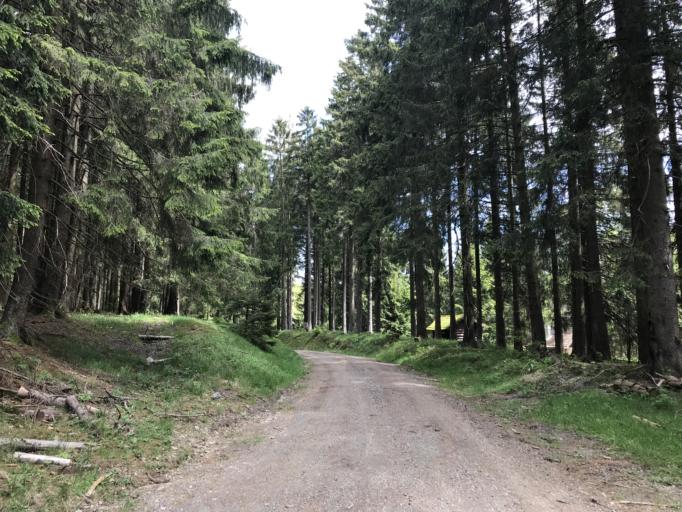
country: DE
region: Lower Saxony
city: Sankt Andreasberg
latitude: 51.7340
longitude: 10.4567
